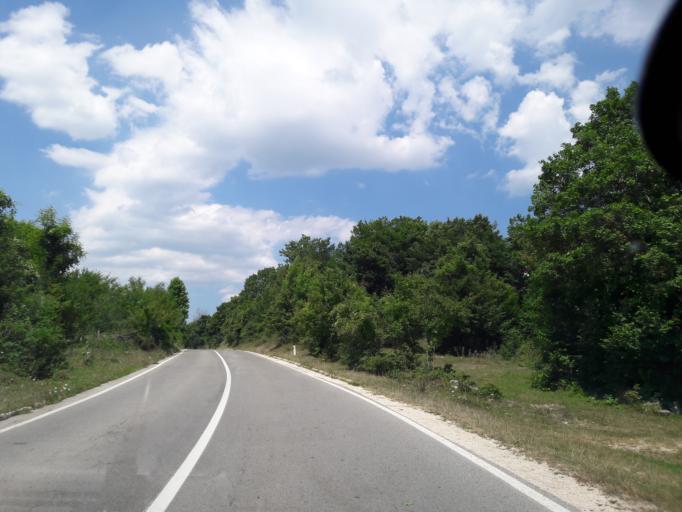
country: BA
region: Republika Srpska
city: Sipovo
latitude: 44.1700
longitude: 17.1680
